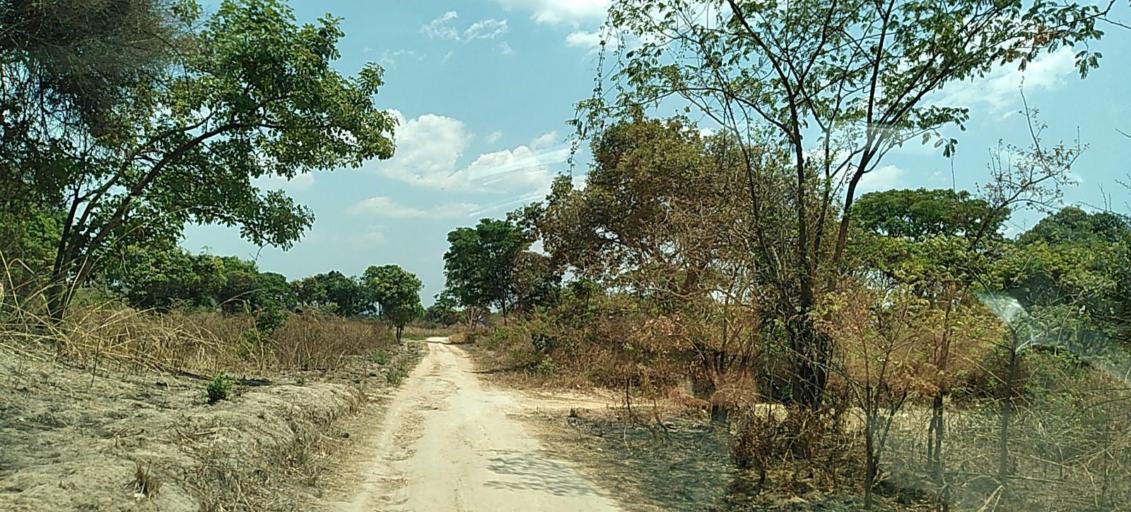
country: ZM
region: Copperbelt
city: Chililabombwe
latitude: -12.4719
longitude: 27.6657
